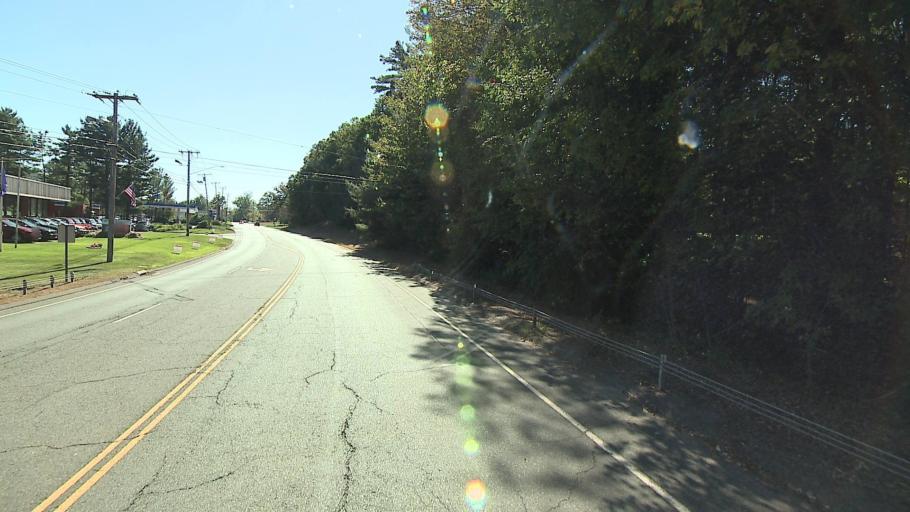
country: US
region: Connecticut
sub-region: Hartford County
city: Weatogue
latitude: 41.8538
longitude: -72.8130
